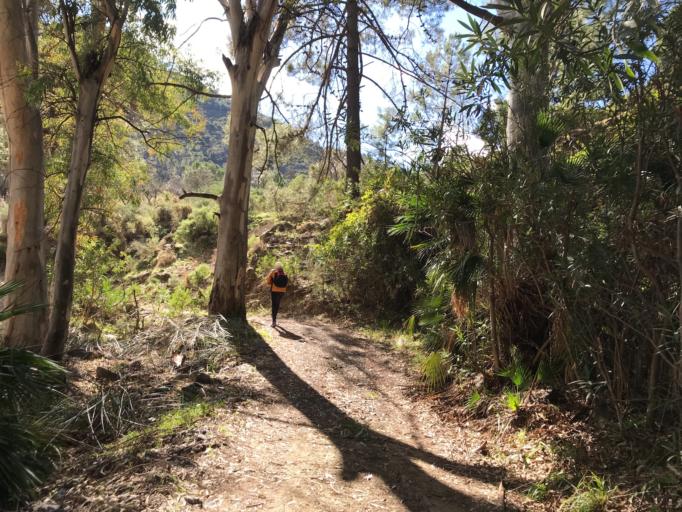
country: ES
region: Andalusia
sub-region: Provincia de Malaga
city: Tolox
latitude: 36.6755
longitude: -4.9155
